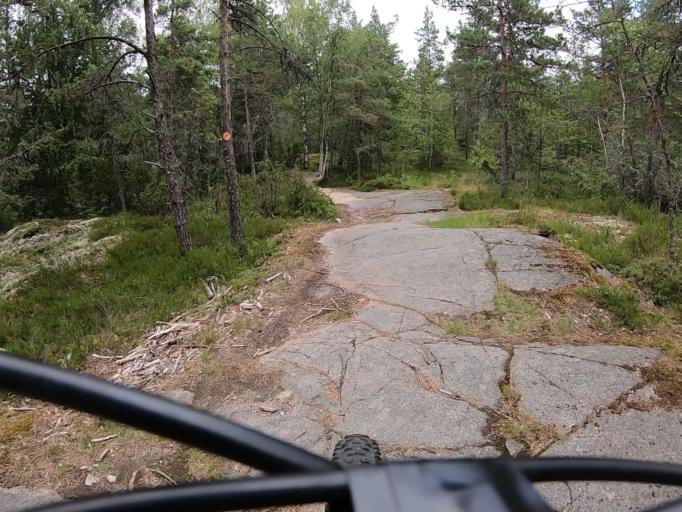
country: FI
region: Varsinais-Suomi
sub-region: Vakka-Suomi
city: Uusikaupunki
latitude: 60.8234
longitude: 21.4133
